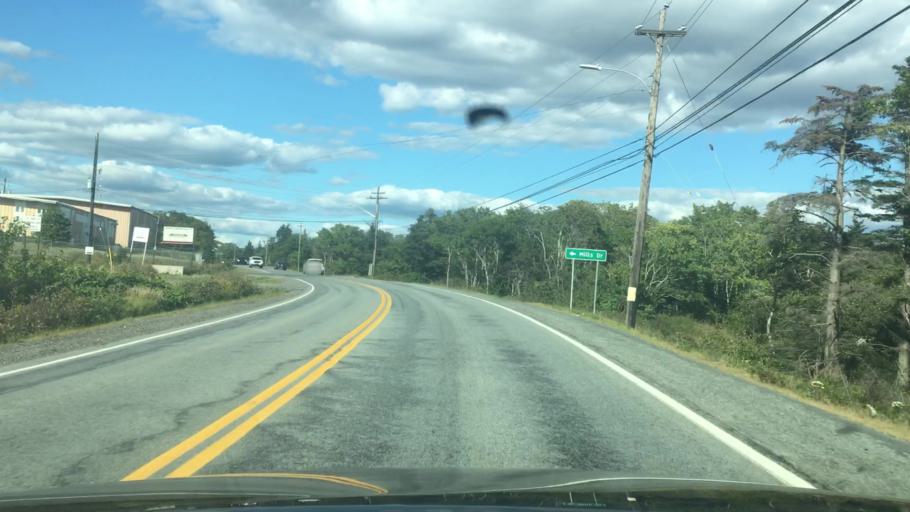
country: CA
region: Nova Scotia
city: Halifax
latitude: 44.6023
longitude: -63.6742
